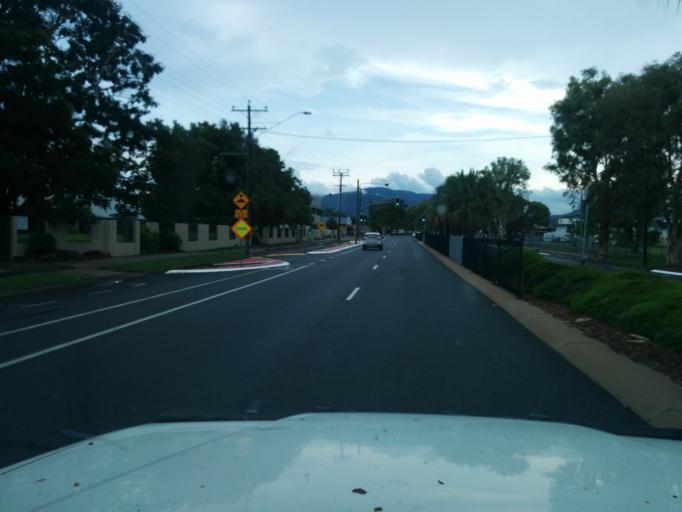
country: AU
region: Queensland
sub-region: Cairns
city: Cairns
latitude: -16.9238
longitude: 145.7513
